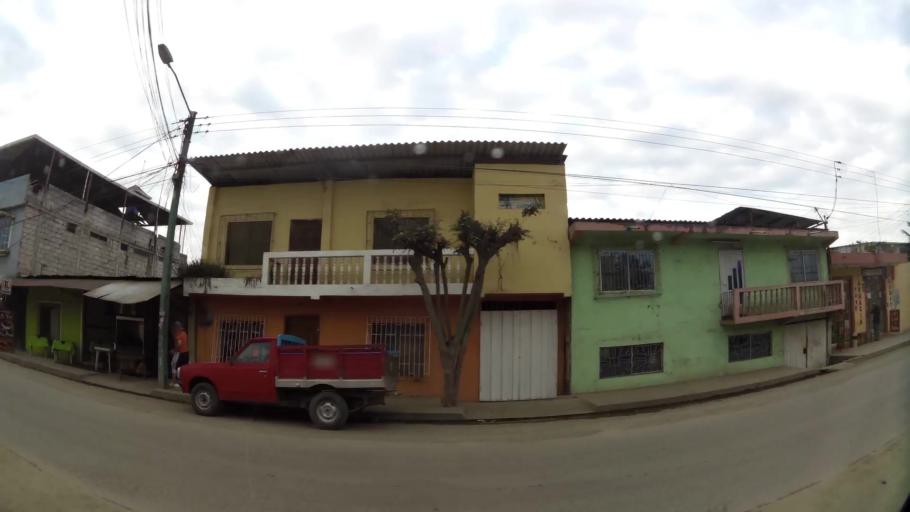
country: EC
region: El Oro
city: Machala
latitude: -3.2682
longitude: -79.9413
